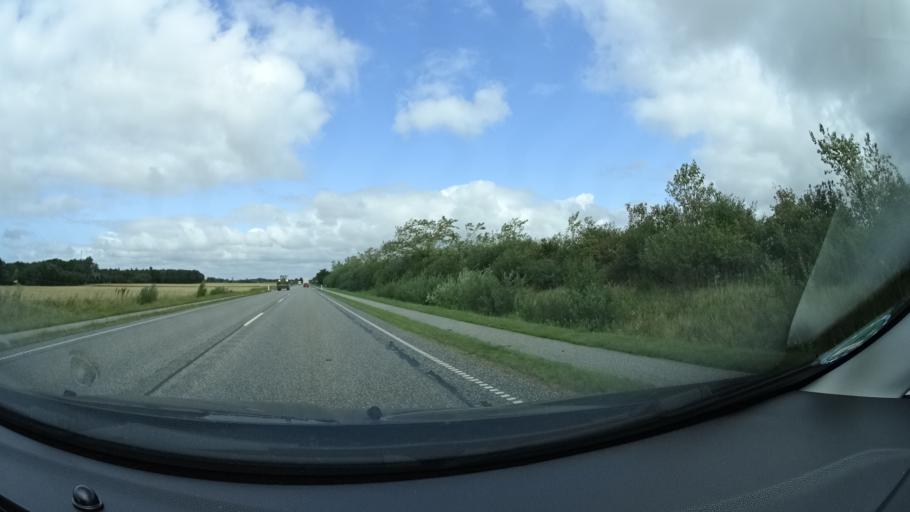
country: DK
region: Central Jutland
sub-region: Ringkobing-Skjern Kommune
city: Ringkobing
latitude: 56.1088
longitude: 8.2625
